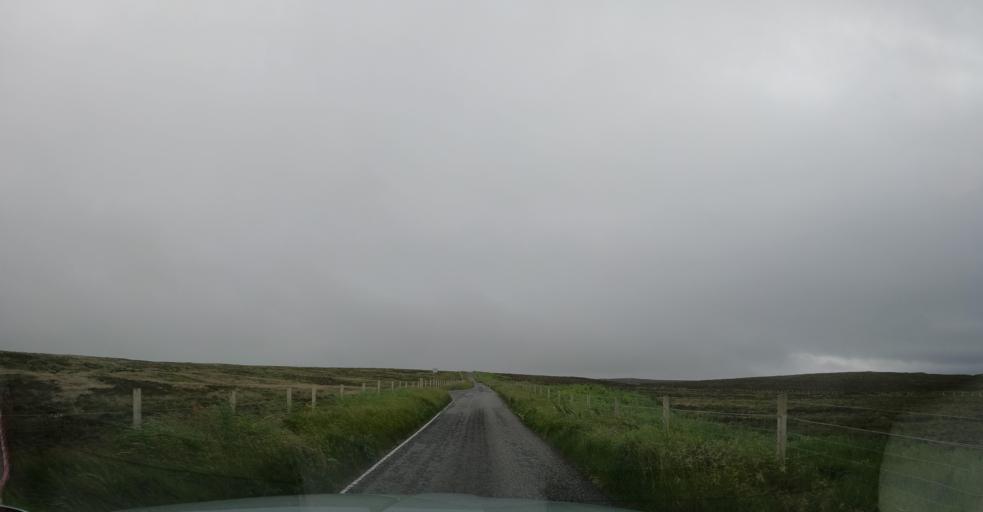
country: GB
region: Scotland
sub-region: Eilean Siar
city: Stornoway
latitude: 58.2073
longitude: -6.2495
